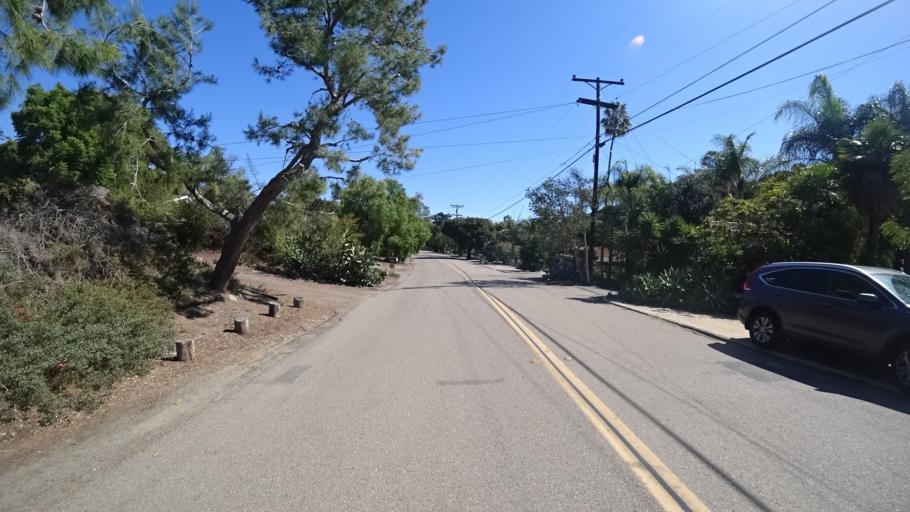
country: US
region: California
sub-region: San Diego County
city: Bonita
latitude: 32.6565
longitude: -117.0105
